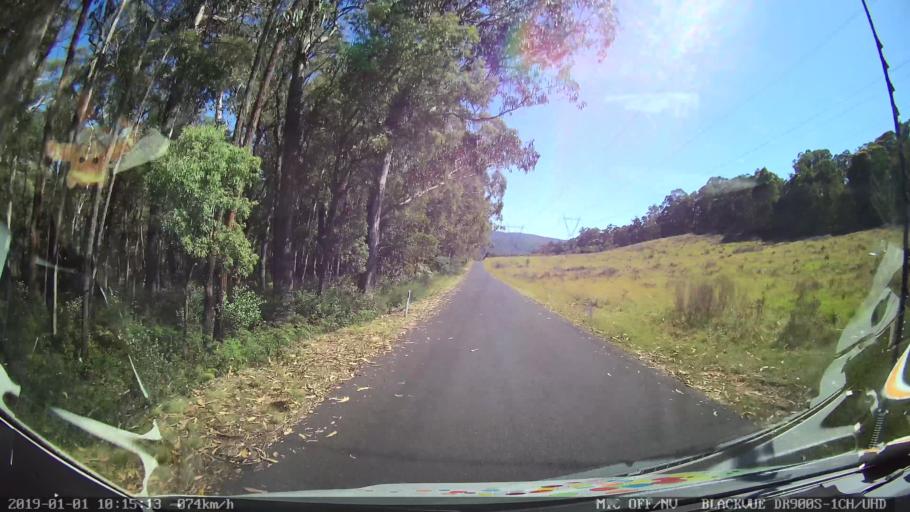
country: AU
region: New South Wales
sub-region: Snowy River
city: Jindabyne
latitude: -36.1043
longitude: 148.1618
